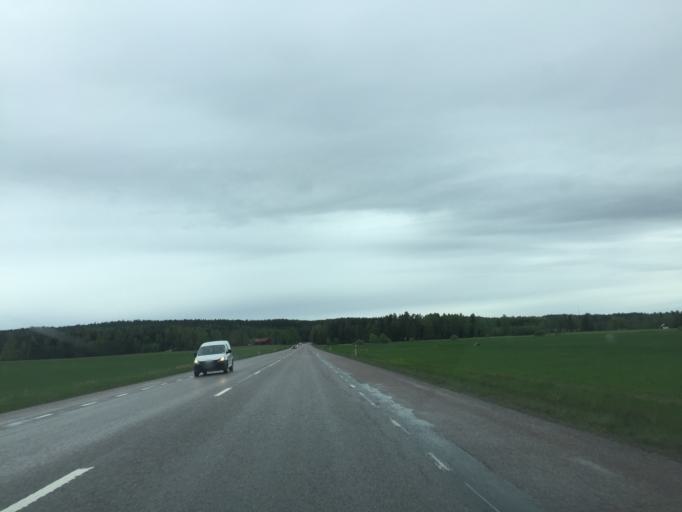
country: SE
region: OErebro
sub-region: Orebro Kommun
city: Hovsta
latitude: 59.4370
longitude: 15.1562
